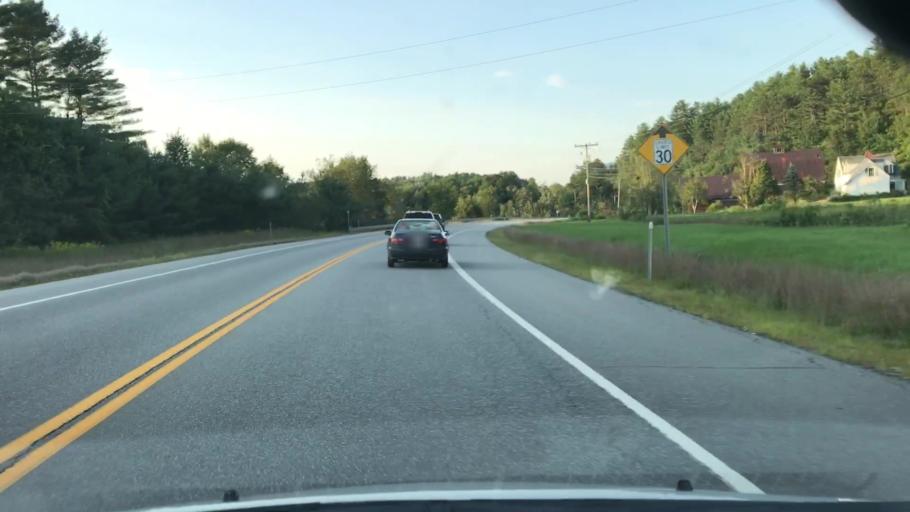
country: US
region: New Hampshire
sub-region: Grafton County
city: Rumney
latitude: 43.8606
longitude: -71.9115
